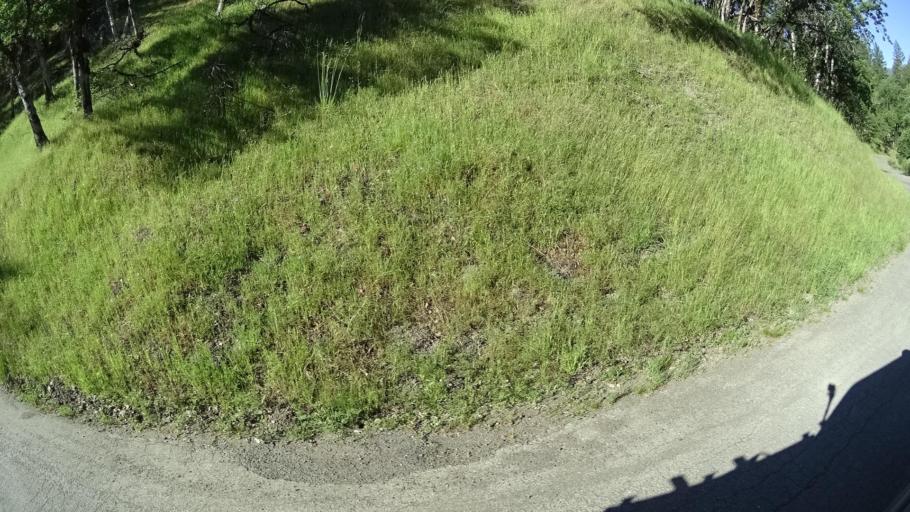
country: US
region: California
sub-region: Lake County
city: Upper Lake
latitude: 39.4086
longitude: -122.9775
